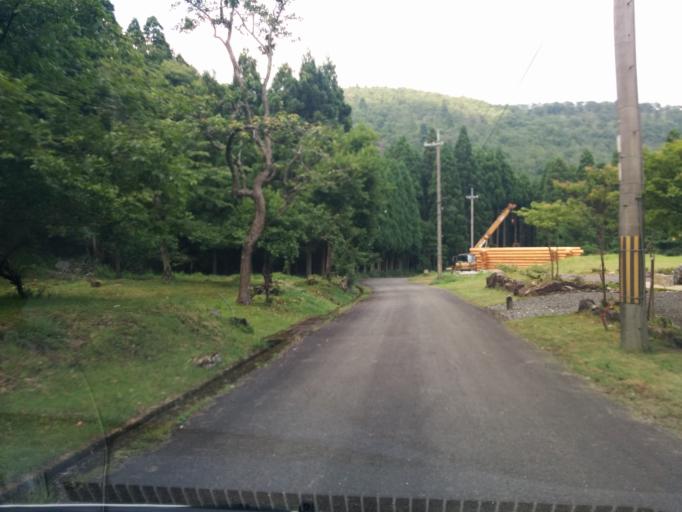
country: JP
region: Kyoto
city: Miyazu
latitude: 35.4596
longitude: 135.1172
